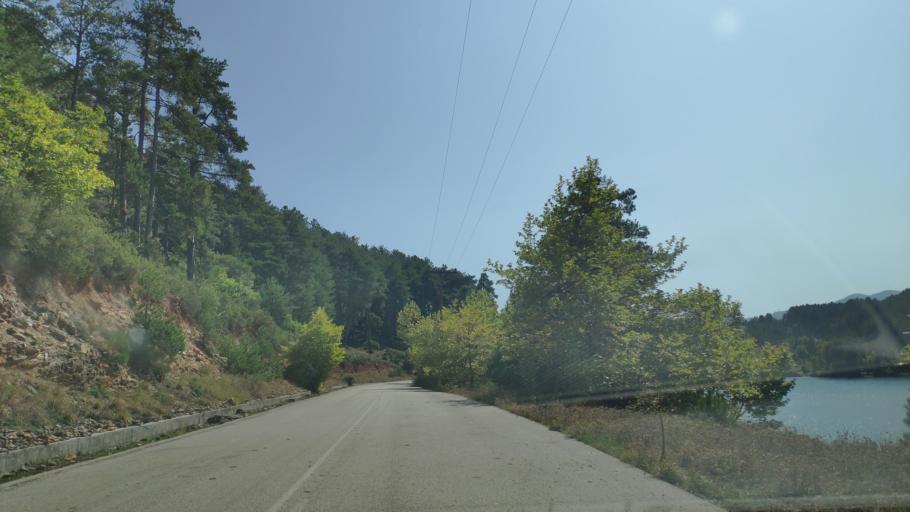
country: GR
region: West Greece
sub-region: Nomos Achaias
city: Kalavryta
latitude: 37.9292
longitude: 22.2905
